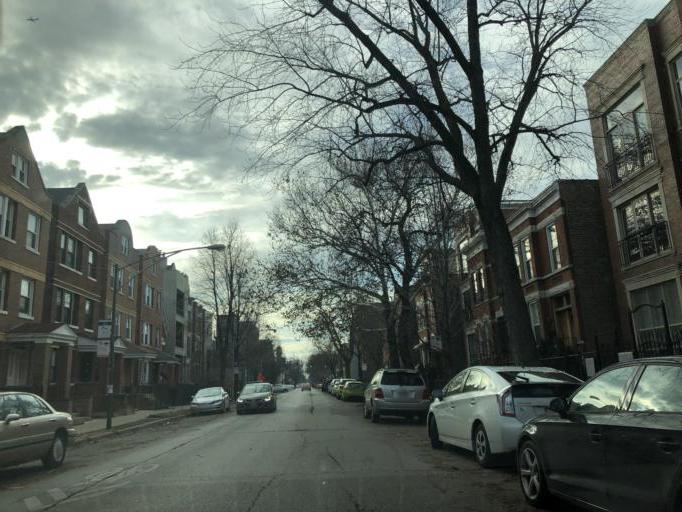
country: US
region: Illinois
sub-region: Cook County
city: Chicago
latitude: 41.9009
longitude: -87.6724
